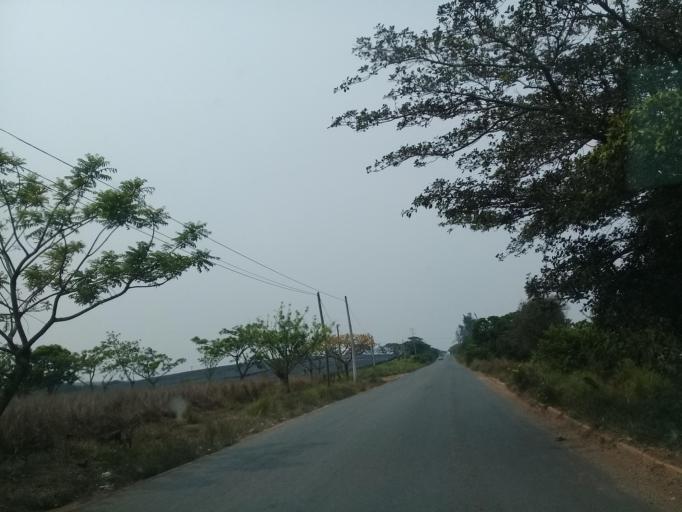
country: MX
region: Veracruz
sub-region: Medellin
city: La Laguna y Monte del Castillo
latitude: 18.9839
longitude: -96.1176
